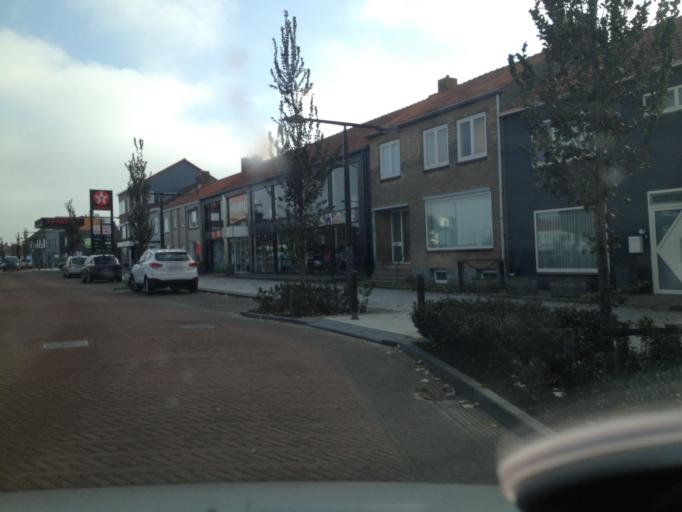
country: NL
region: Zeeland
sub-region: Gemeente Vlissingen
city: Vlissingen
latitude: 51.3960
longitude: 3.5588
